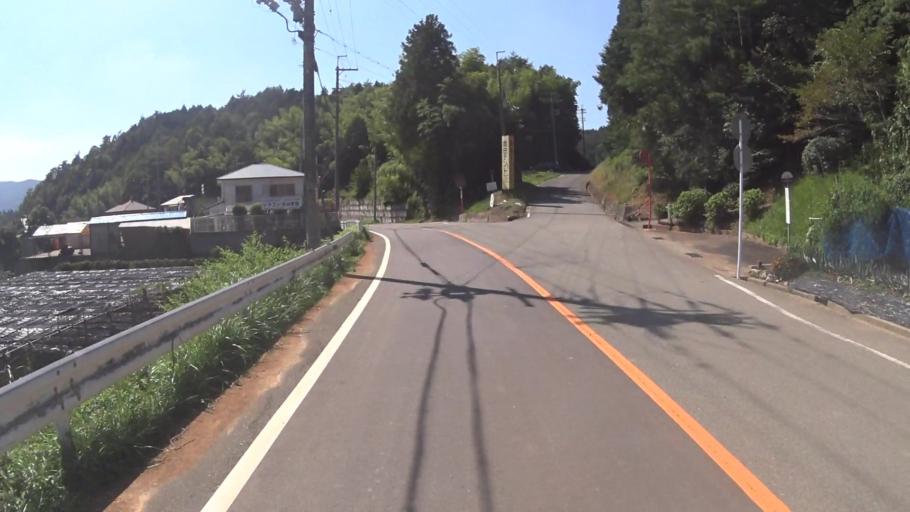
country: JP
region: Kyoto
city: Kameoka
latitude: 34.9726
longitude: 135.5072
